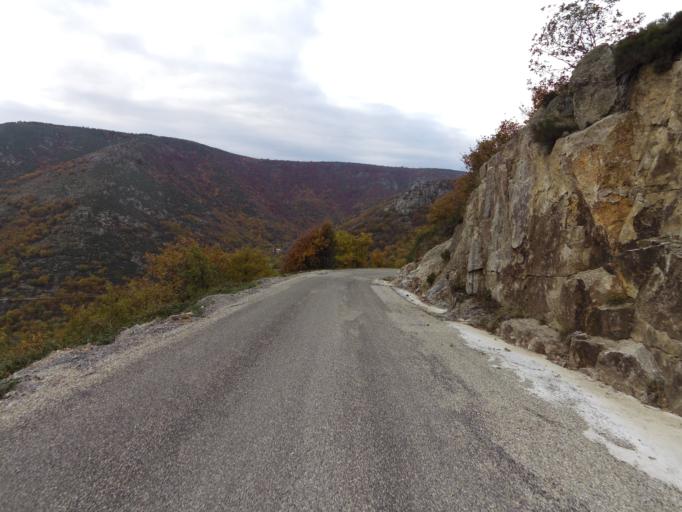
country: FR
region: Rhone-Alpes
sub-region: Departement de l'Ardeche
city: Les Vans
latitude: 44.5068
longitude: 4.0391
